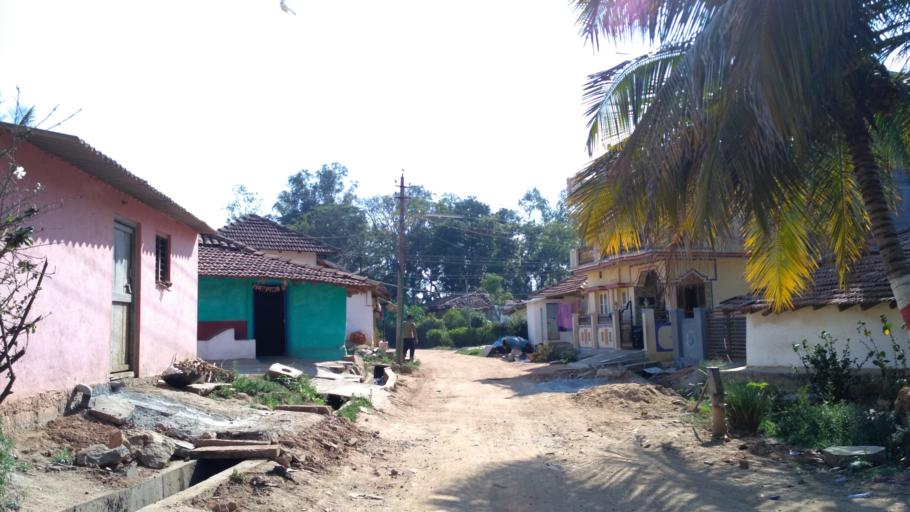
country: IN
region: Karnataka
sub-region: Hassan
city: Hassan
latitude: 12.9996
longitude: 76.1239
